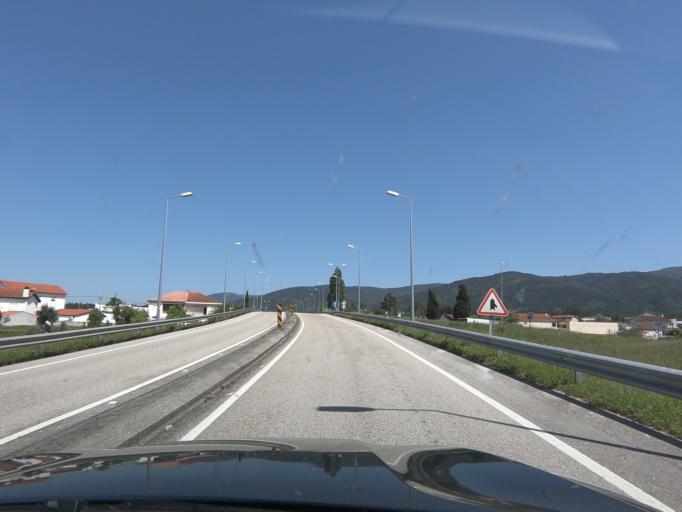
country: PT
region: Coimbra
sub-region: Miranda do Corvo
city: Miranda do Corvo
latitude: 40.0834
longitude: -8.3293
